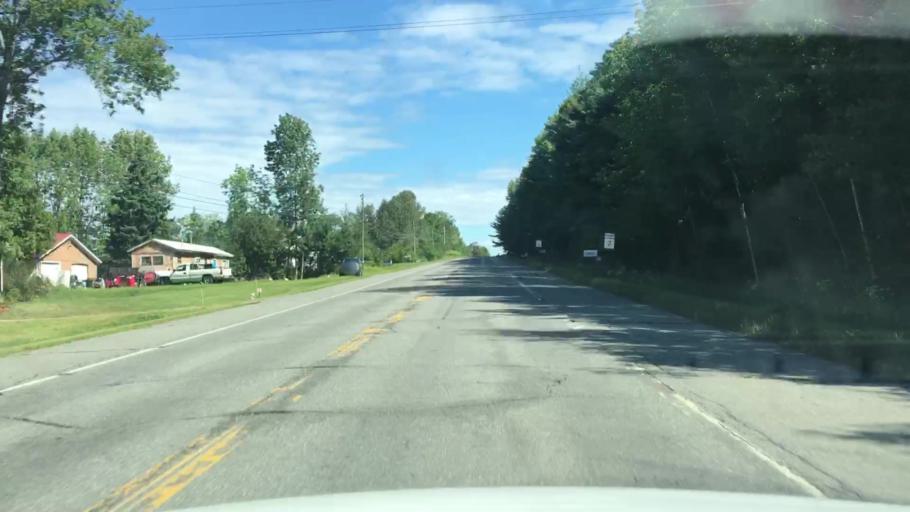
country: US
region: Maine
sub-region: Penobscot County
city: Dexter
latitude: 45.0570
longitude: -69.2544
